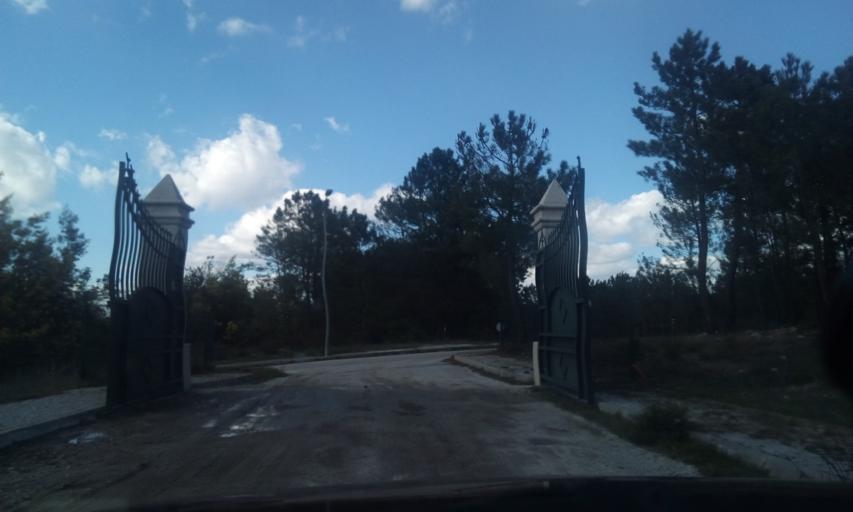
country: PT
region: Guarda
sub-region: Fornos de Algodres
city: Fornos de Algodres
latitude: 40.6240
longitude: -7.5447
